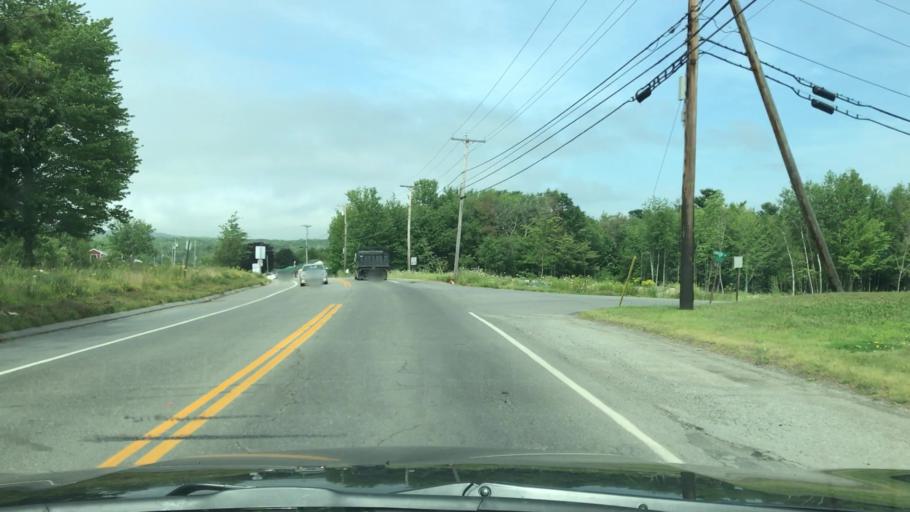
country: US
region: Maine
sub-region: Waldo County
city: Stockton Springs
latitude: 44.4638
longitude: -68.9042
